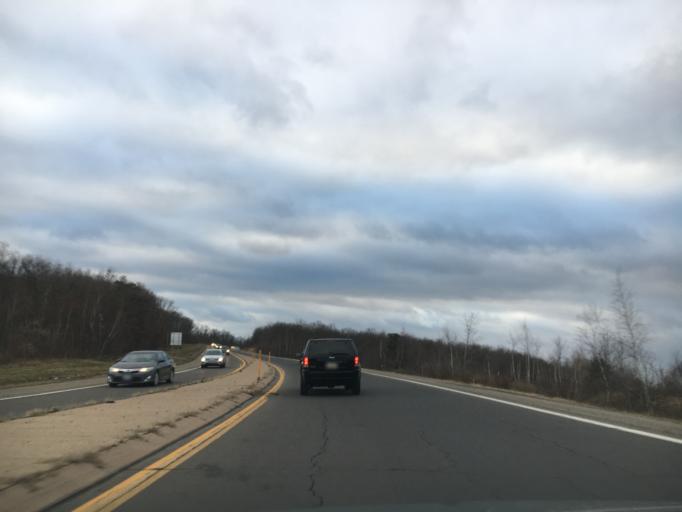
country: US
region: Pennsylvania
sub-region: Schuylkill County
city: McAdoo
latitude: 40.9307
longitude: -75.9960
